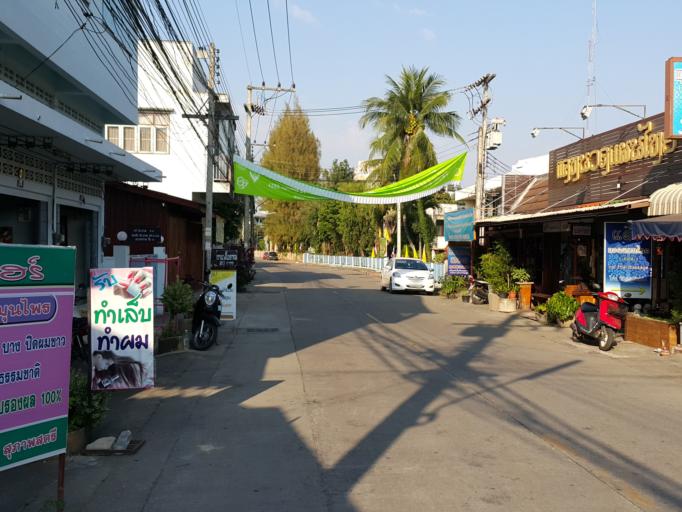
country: TH
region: Lampang
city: Lampang
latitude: 18.2846
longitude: 99.5085
